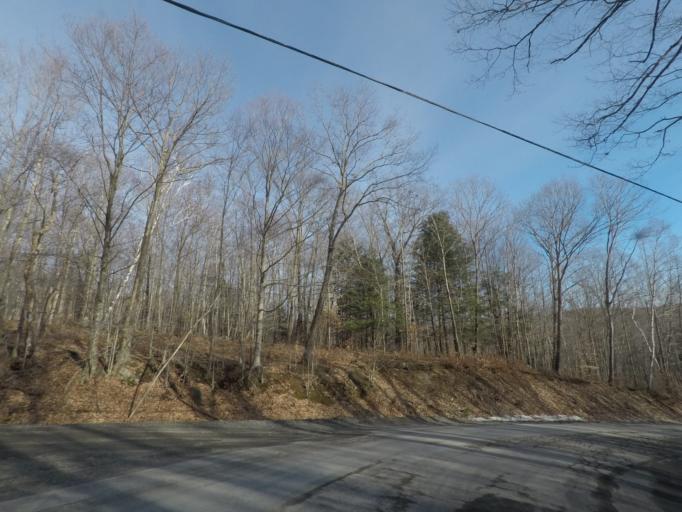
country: US
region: New York
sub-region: Rensselaer County
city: Hoosick Falls
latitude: 42.7385
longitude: -73.3811
